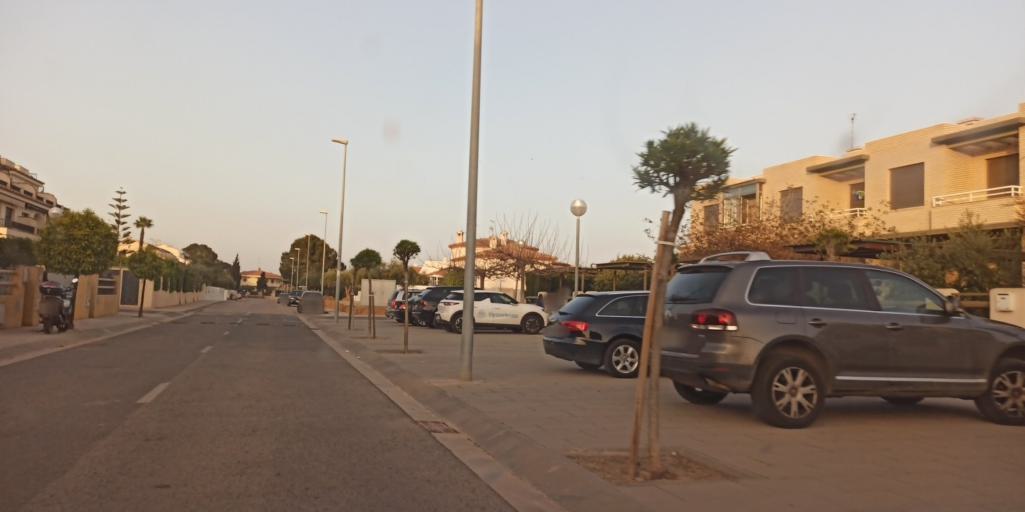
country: ES
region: Catalonia
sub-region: Provincia de Tarragona
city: L'Ampolla
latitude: 40.8216
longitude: 0.7272
